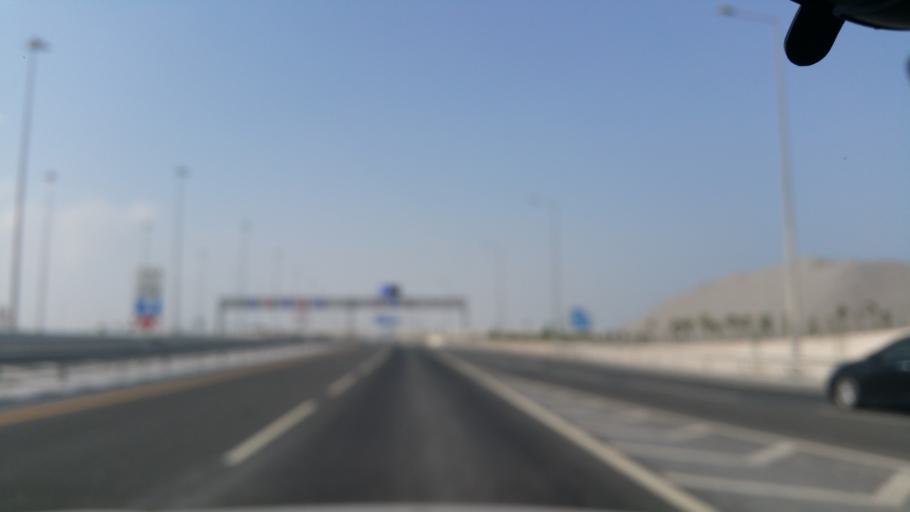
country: QA
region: Baladiyat Umm Salal
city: Umm Salal Muhammad
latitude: 25.4495
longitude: 51.4803
